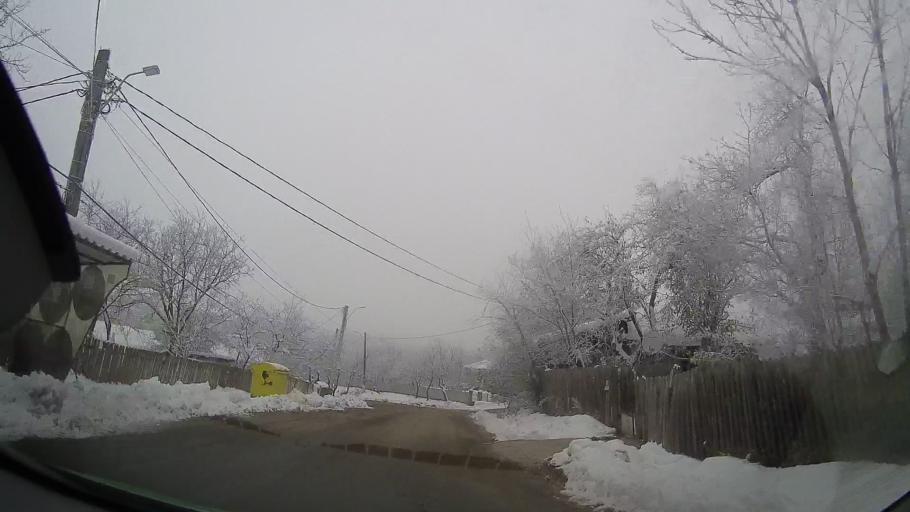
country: RO
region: Iasi
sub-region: Comuna Tansa
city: Tansa
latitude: 46.9079
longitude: 27.2411
